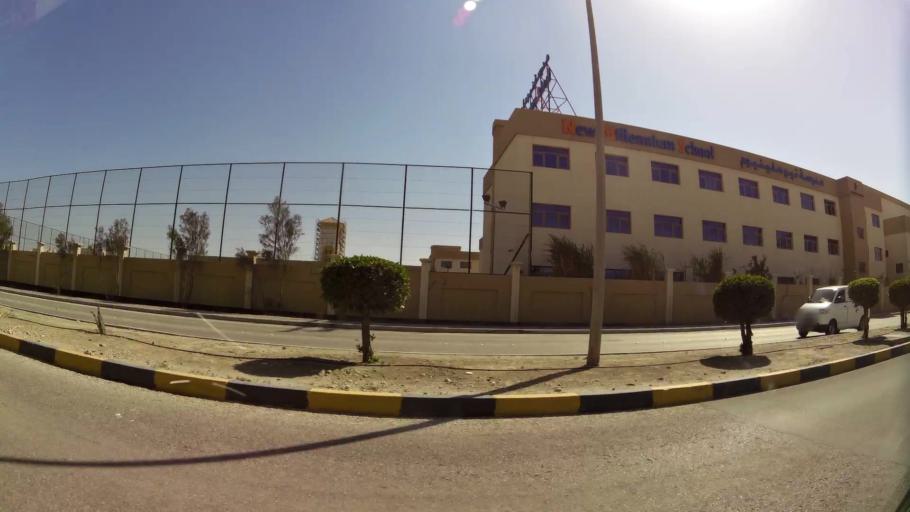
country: BH
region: Manama
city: Manama
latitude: 26.2125
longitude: 50.5728
